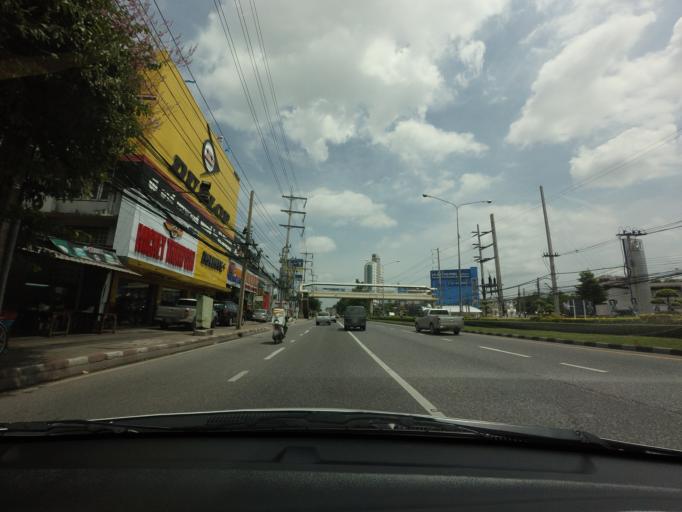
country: TH
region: Bangkok
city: Khan Na Yao
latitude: 13.8367
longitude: 100.6646
